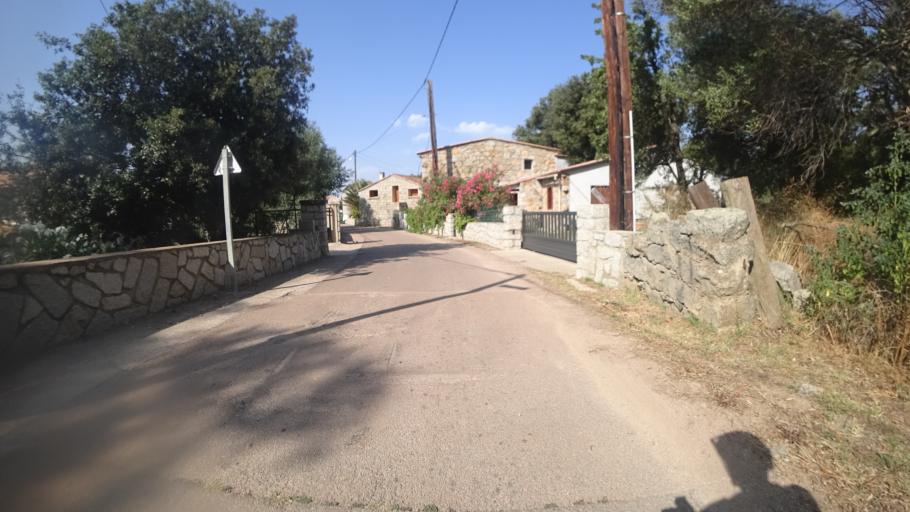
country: FR
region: Corsica
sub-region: Departement de la Corse-du-Sud
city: Porto-Vecchio
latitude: 41.6629
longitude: 9.3285
